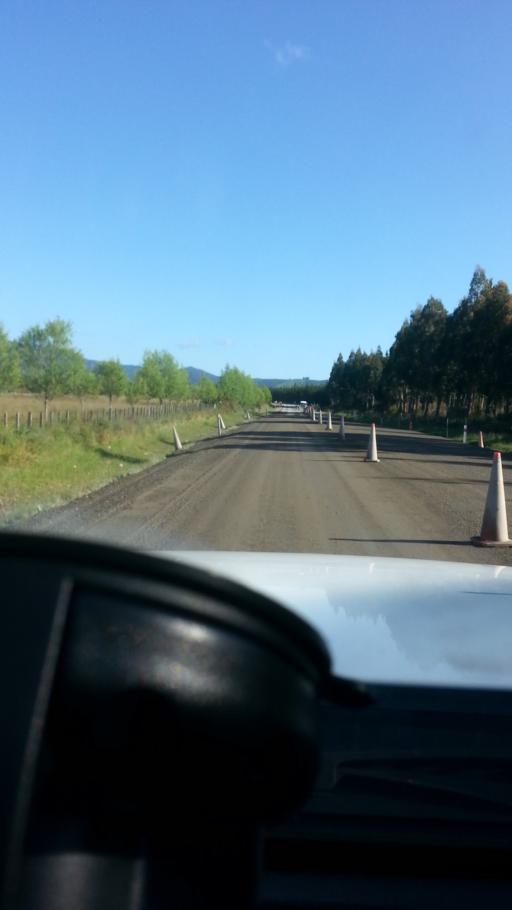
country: NZ
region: Wellington
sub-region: Masterton District
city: Masterton
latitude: -40.8065
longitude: 175.6198
